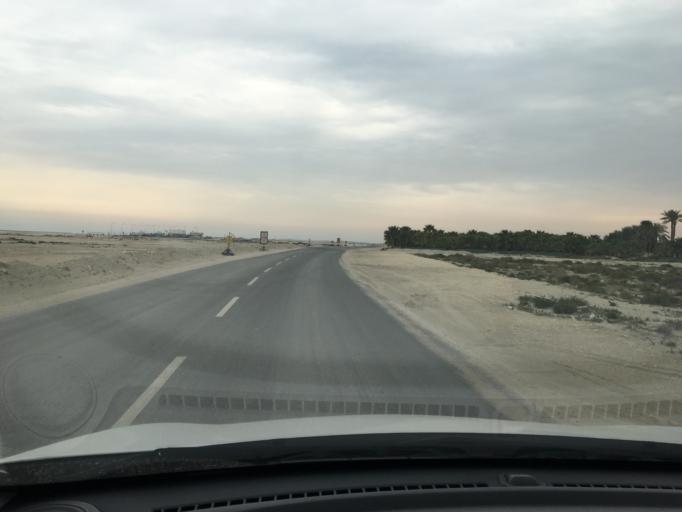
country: BH
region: Central Governorate
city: Dar Kulayb
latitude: 25.8381
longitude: 50.5876
